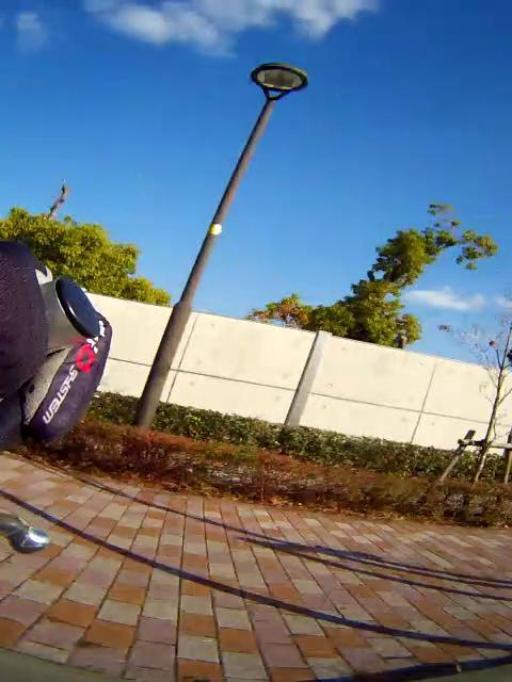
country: JP
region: Hyogo
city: Takarazuka
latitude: 34.7787
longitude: 135.3577
